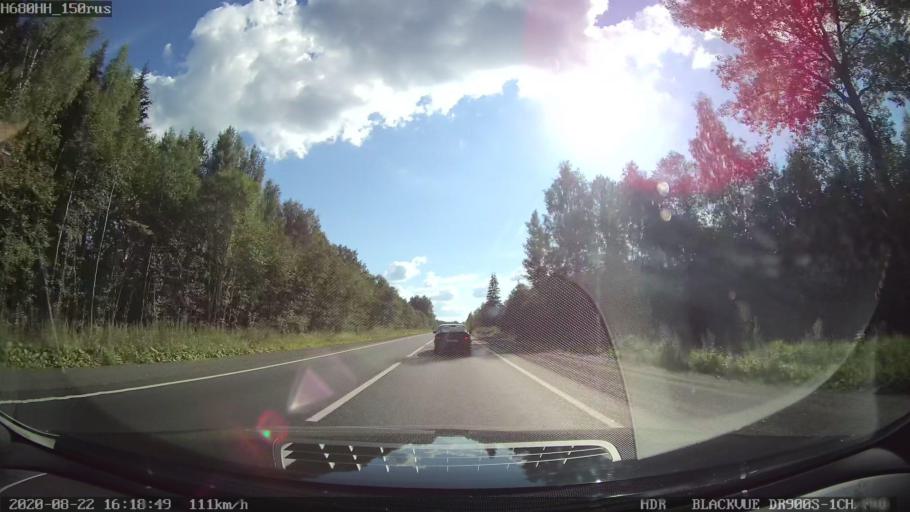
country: RU
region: Tverskaya
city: Rameshki
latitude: 57.4115
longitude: 36.1319
